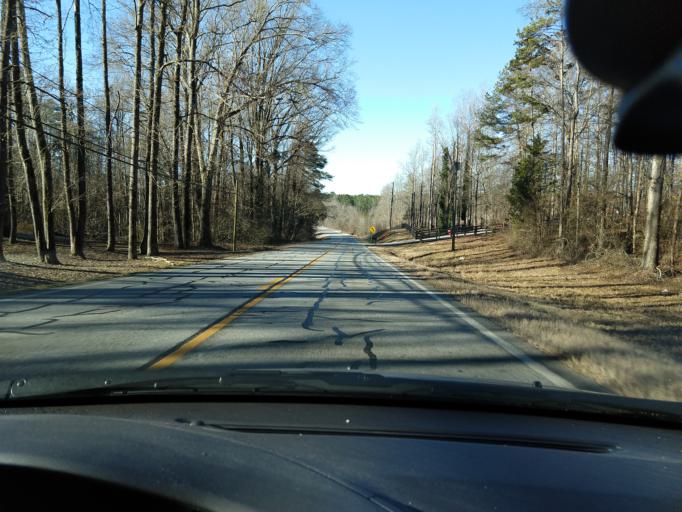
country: US
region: Georgia
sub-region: Jackson County
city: Jefferson
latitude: 34.1542
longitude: -83.5161
